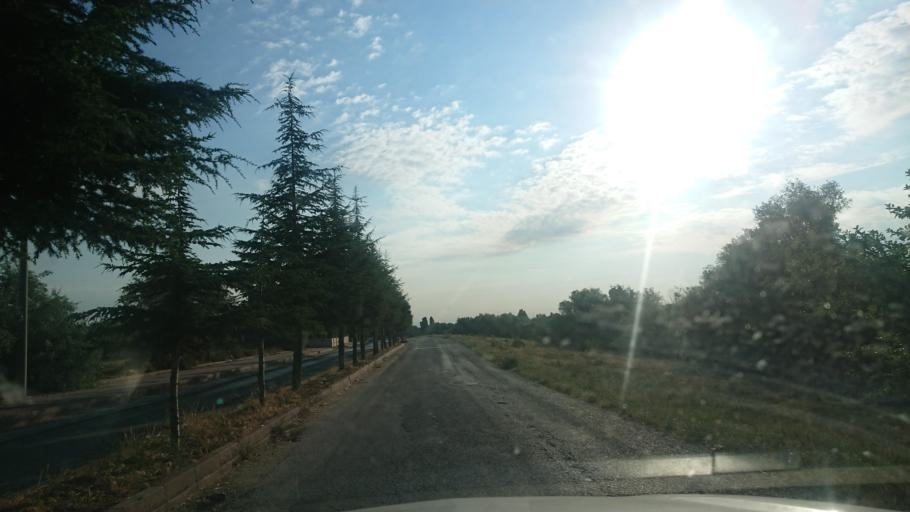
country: TR
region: Aksaray
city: Ortakoy
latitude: 38.7466
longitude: 34.0500
